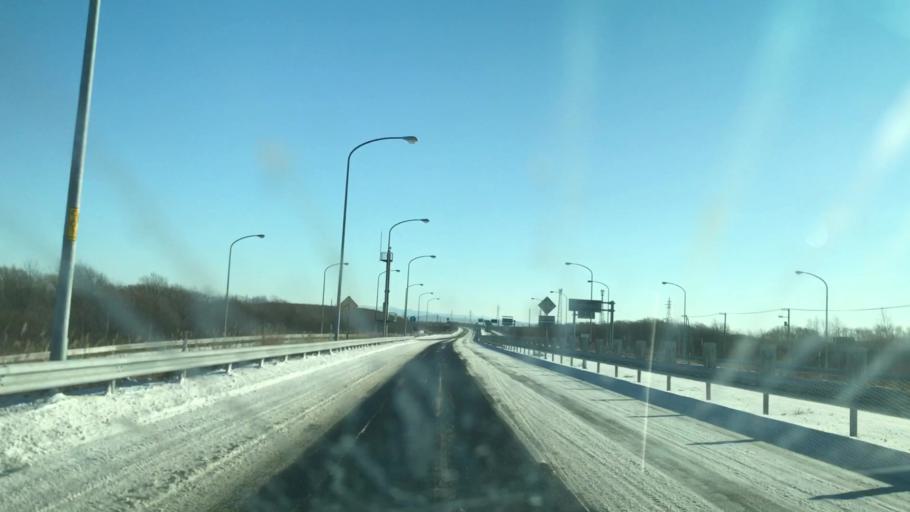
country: JP
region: Hokkaido
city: Tomakomai
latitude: 42.6749
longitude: 141.7340
